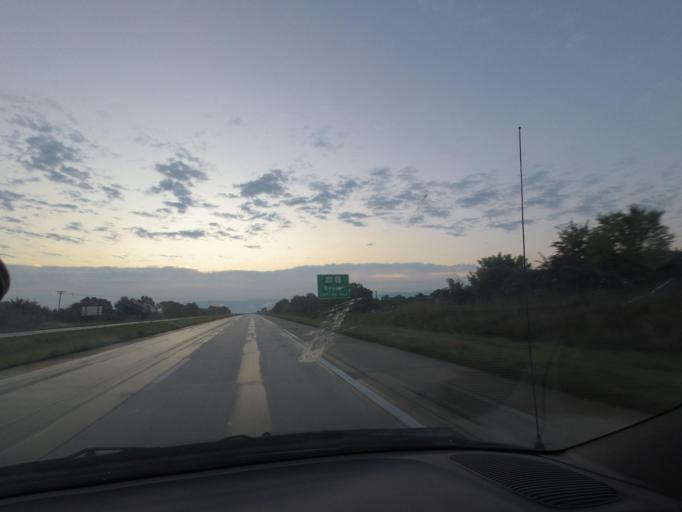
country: US
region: Missouri
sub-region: Macon County
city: Macon
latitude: 39.7606
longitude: -92.5768
